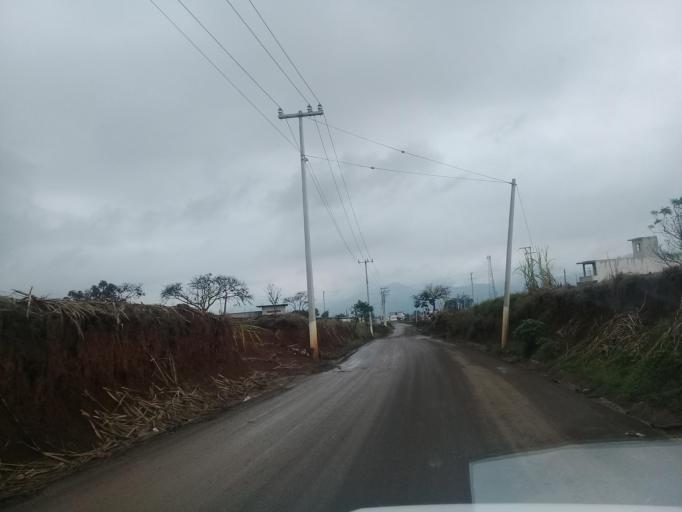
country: MX
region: Veracruz
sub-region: Cordoba
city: Veinte de Noviembre
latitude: 18.8581
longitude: -96.9591
